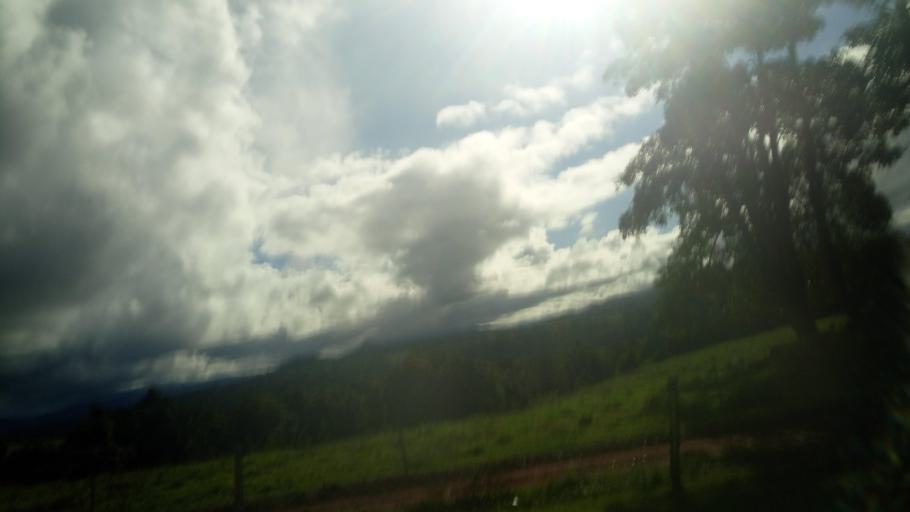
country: AU
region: Queensland
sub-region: Cassowary Coast
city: Innisfail
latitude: -17.5402
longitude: 145.9636
